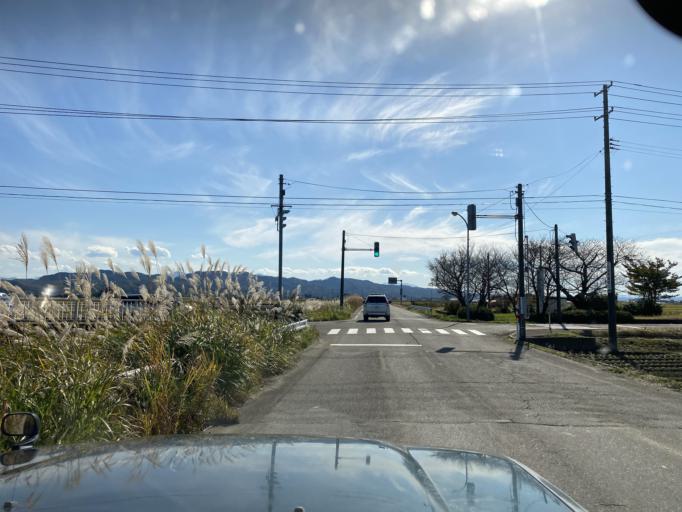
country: JP
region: Niigata
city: Niitsu-honcho
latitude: 37.7734
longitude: 139.0832
